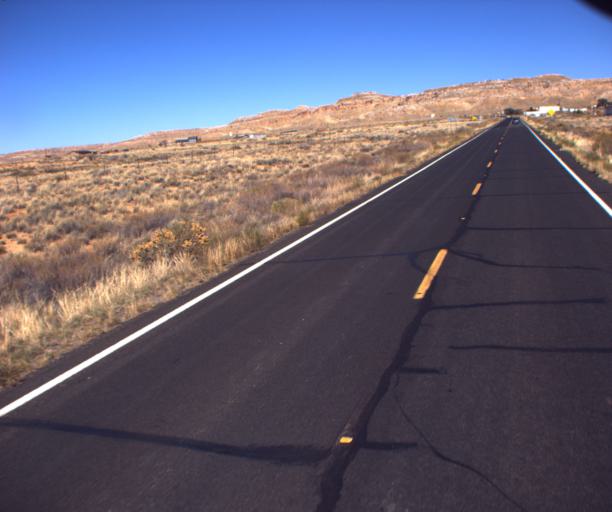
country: US
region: Arizona
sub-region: Navajo County
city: First Mesa
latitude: 35.7854
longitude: -110.4995
